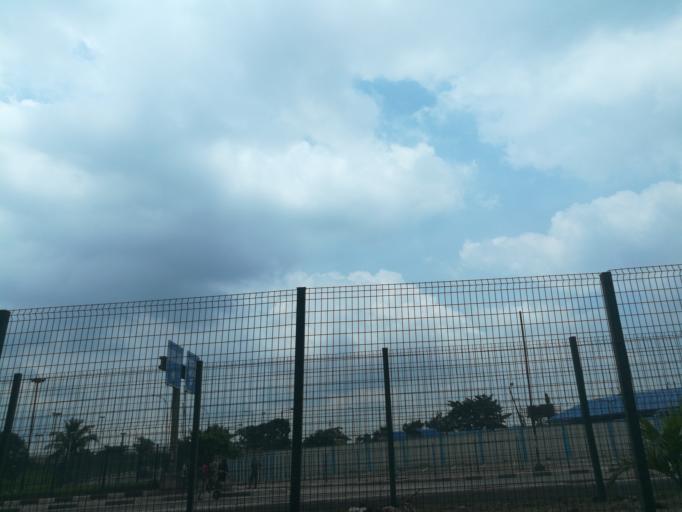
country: NG
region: Lagos
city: Ojota
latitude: 6.5926
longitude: 3.3824
